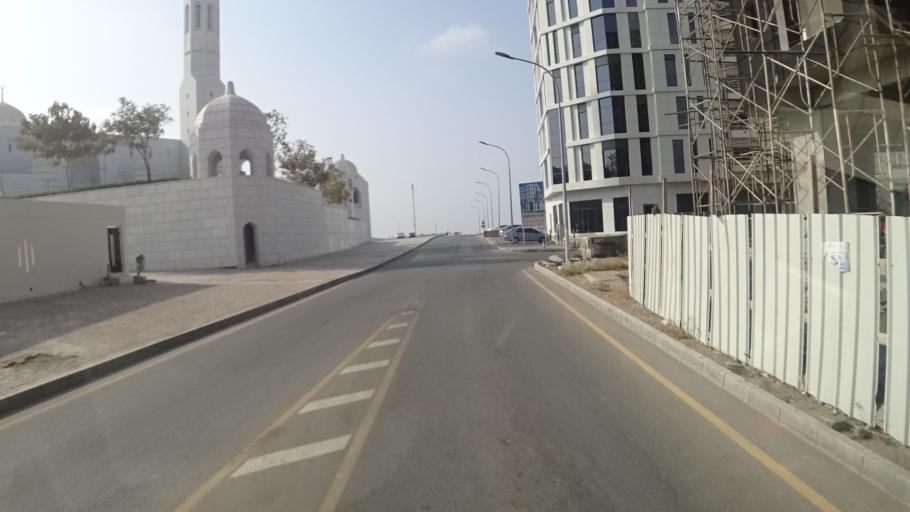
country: OM
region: Muhafazat Masqat
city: Bawshar
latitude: 23.5782
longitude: 58.4157
